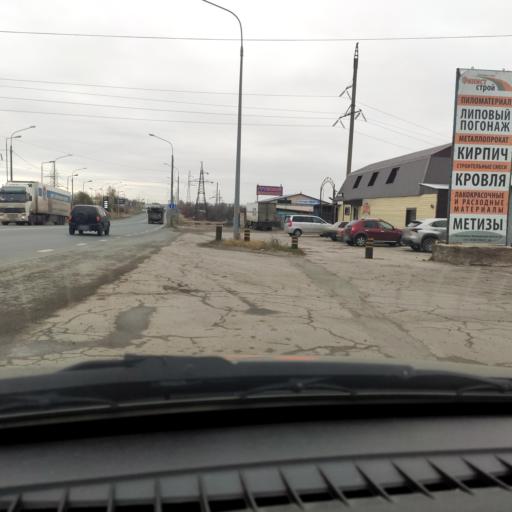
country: RU
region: Samara
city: Zhigulevsk
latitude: 53.3844
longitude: 49.4555
